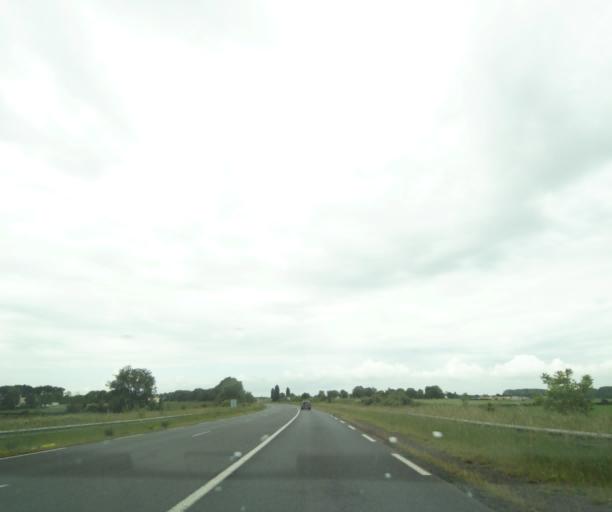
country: FR
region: Poitou-Charentes
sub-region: Departement des Deux-Sevres
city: Airvault
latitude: 46.8213
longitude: -0.2043
